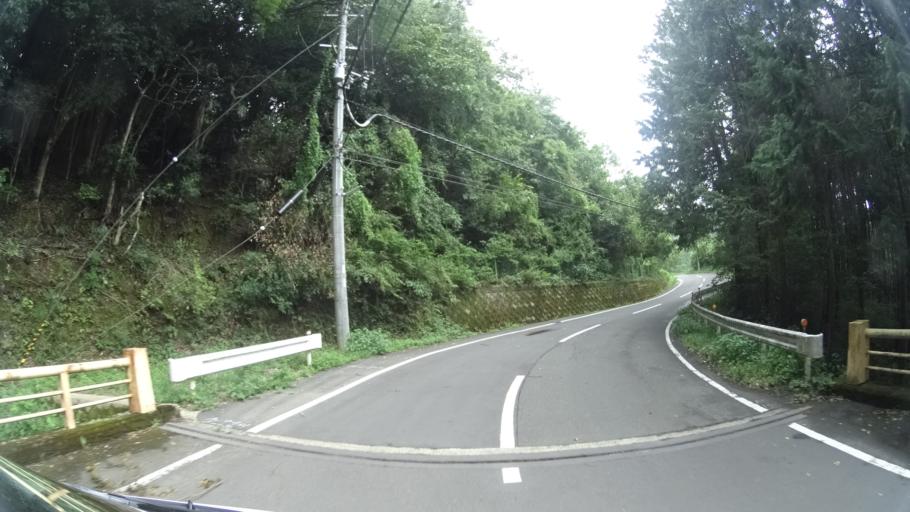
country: JP
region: Kyoto
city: Ayabe
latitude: 35.2803
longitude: 135.3303
